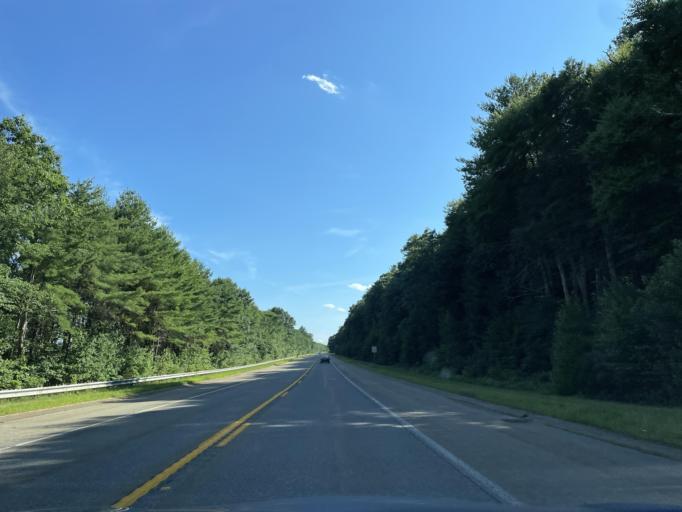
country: US
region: Massachusetts
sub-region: Worcester County
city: Sturbridge
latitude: 42.1491
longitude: -72.0382
